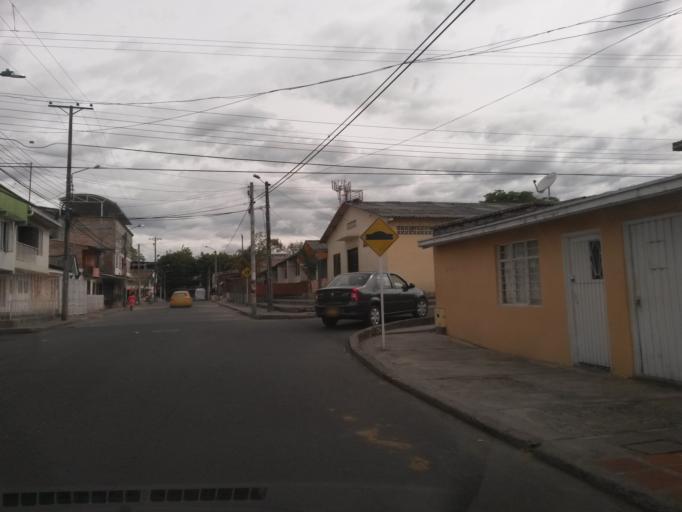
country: CO
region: Cauca
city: Popayan
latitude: 2.4473
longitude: -76.6159
